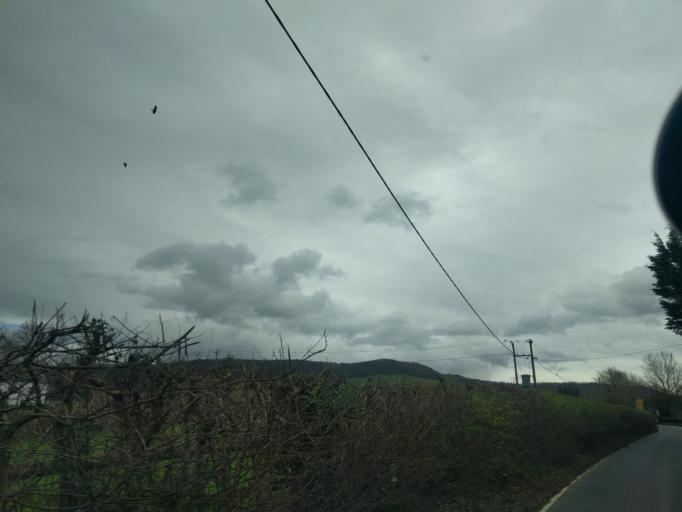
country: GB
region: England
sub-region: Gloucestershire
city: Stonehouse
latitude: 51.7266
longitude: -2.3118
